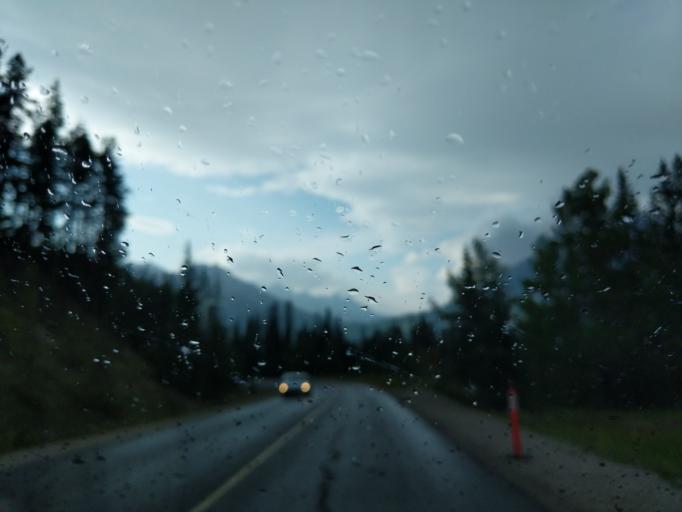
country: CA
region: Alberta
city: Banff
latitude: 51.1590
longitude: -115.5658
